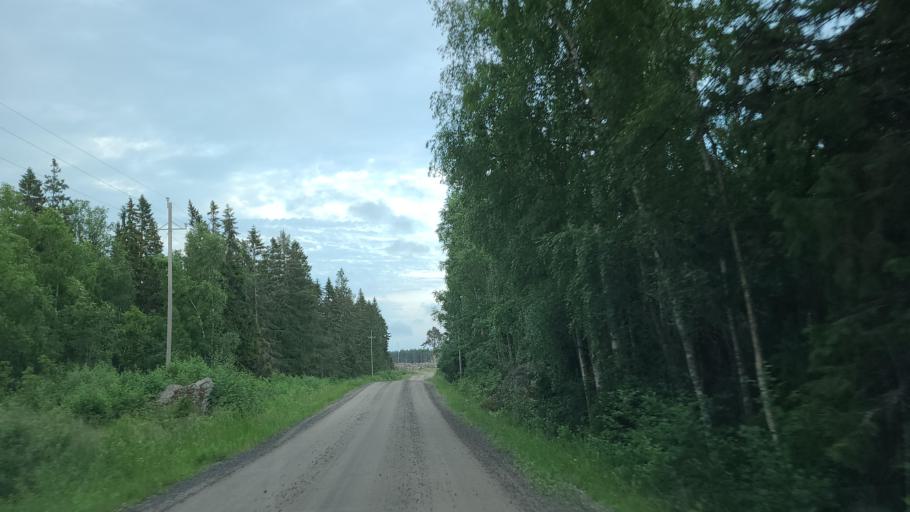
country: FI
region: Ostrobothnia
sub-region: Vaasa
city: Replot
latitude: 63.3208
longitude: 21.1444
